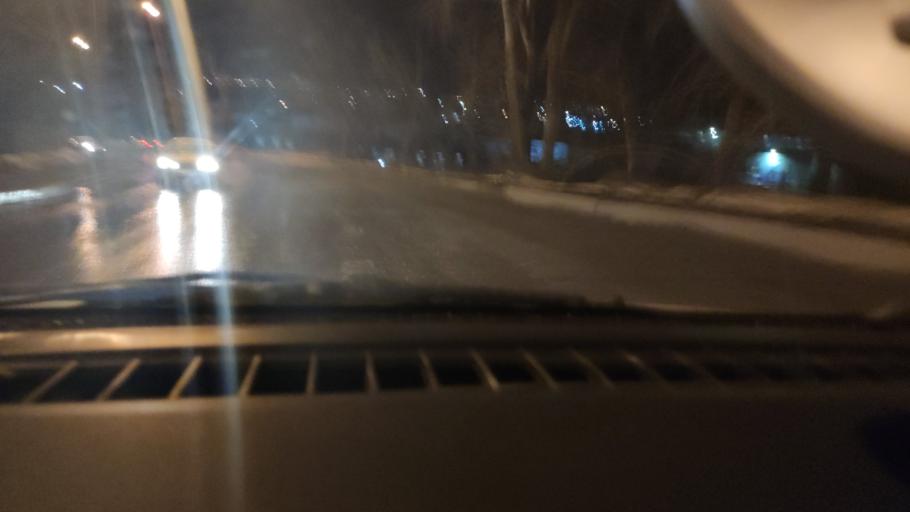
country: RU
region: Perm
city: Perm
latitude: 58.0707
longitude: 56.3525
